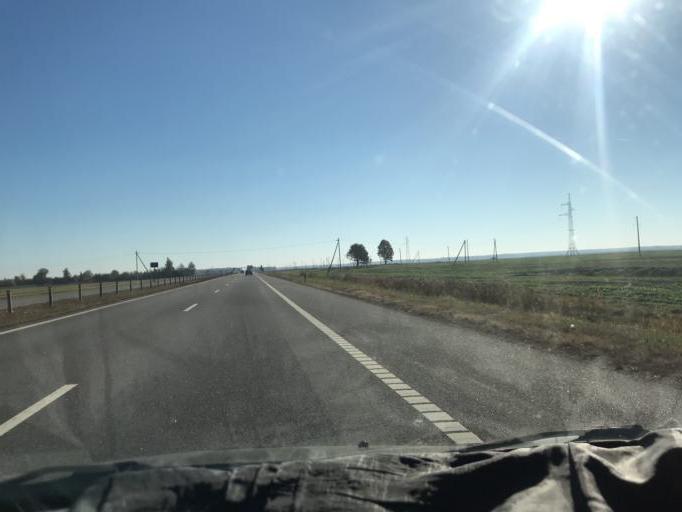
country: BY
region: Mogilev
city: Yalizava
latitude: 53.2368
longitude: 28.9685
